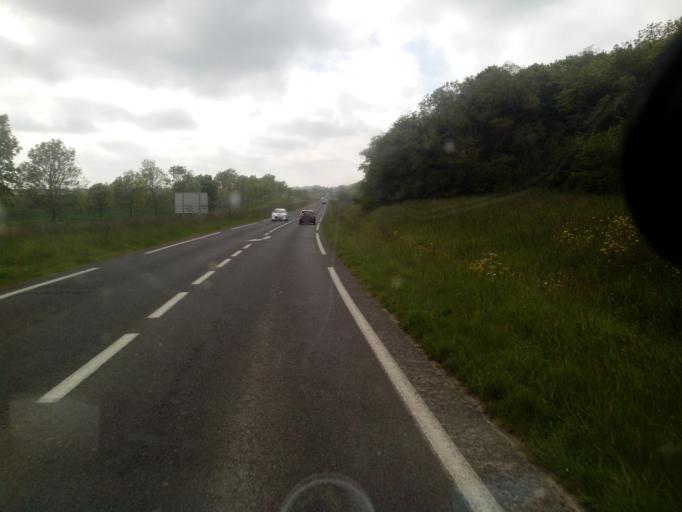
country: FR
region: Lower Normandy
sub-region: Departement du Calvados
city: Douvres-la-Delivrande
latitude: 49.2754
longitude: -0.3811
